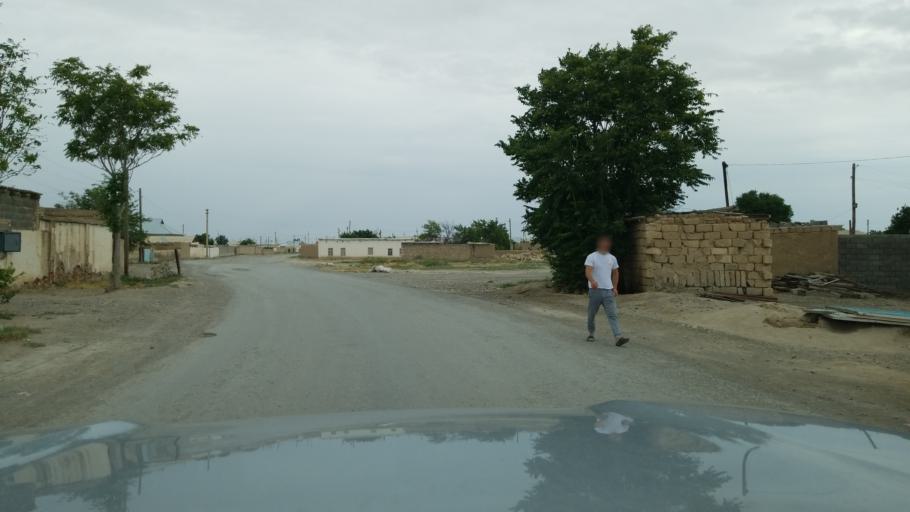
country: TM
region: Balkan
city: Serdar
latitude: 38.9887
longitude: 56.2774
